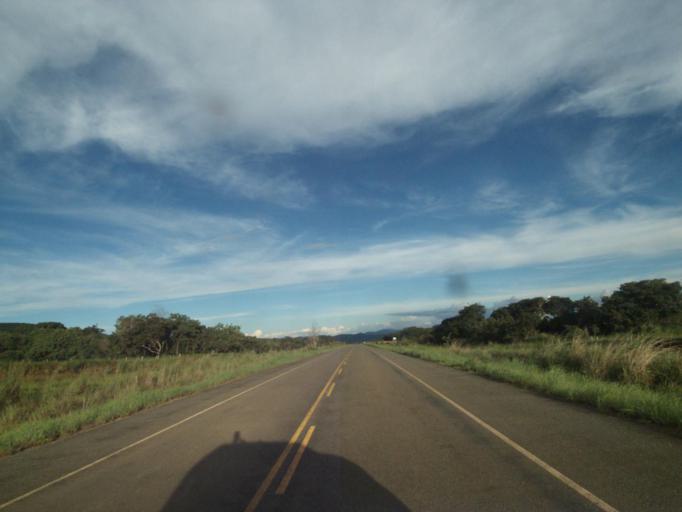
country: BR
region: Goias
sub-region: Jaragua
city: Jaragua
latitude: -15.8377
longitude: -49.3110
